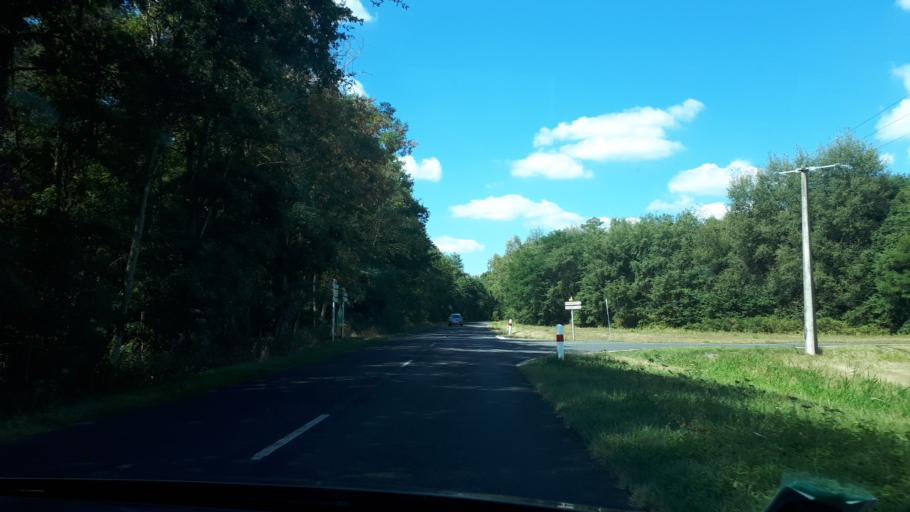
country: FR
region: Centre
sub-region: Departement du Loir-et-Cher
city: Neung-sur-Beuvron
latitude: 47.5340
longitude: 1.7496
